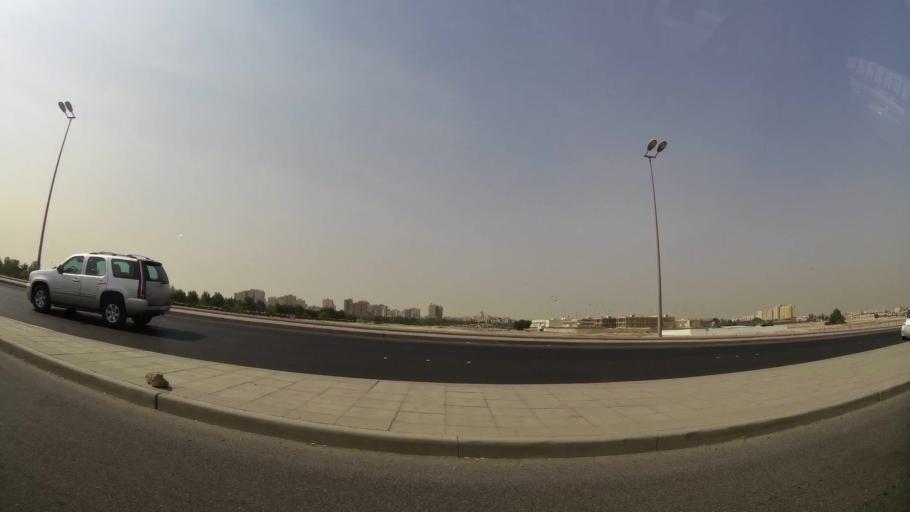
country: KW
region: Al Farwaniyah
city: Al Farwaniyah
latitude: 29.2606
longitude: 47.9530
